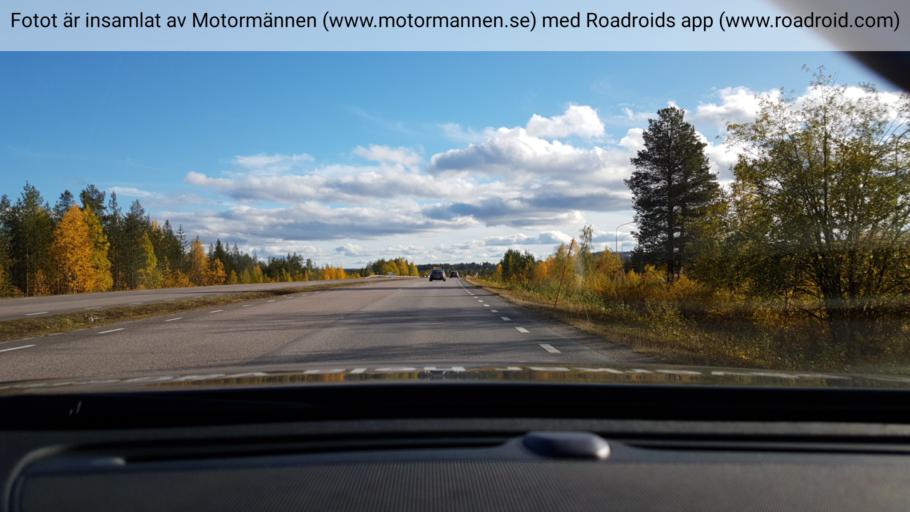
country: SE
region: Norrbotten
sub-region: Gallivare Kommun
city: Malmberget
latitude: 67.1584
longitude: 20.6592
